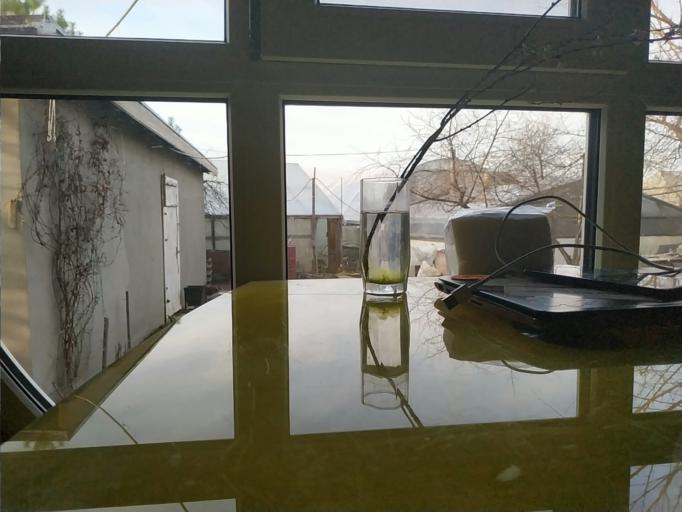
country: RU
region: Republic of Karelia
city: Suoyarvi
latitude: 62.0598
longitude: 32.1823
